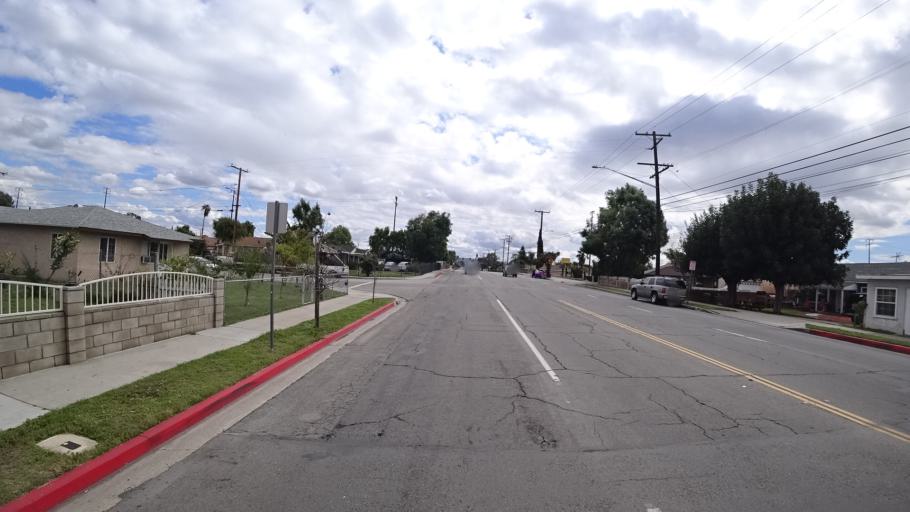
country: US
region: California
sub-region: Los Angeles County
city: Baldwin Park
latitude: 34.0824
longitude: -117.9566
